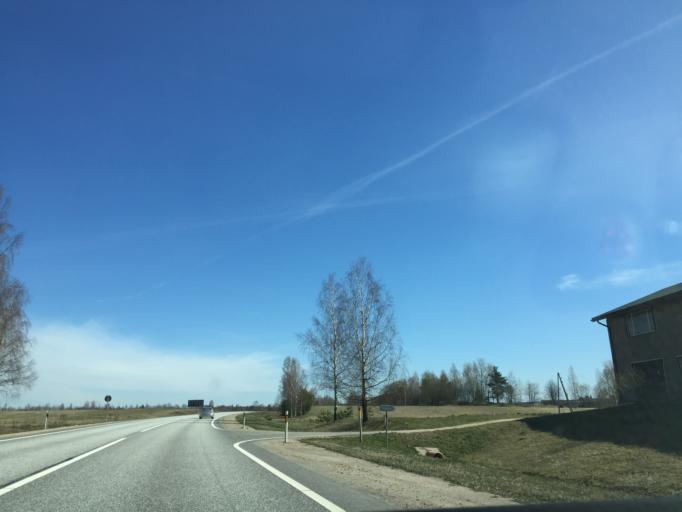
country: LV
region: Valmieras Rajons
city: Valmiera
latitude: 57.5487
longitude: 25.3903
